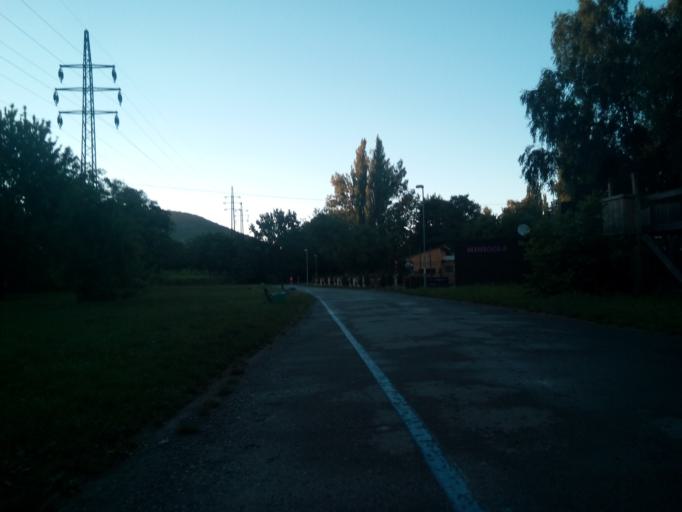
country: SK
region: Kosicky
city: Kosice
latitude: 48.7463
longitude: 21.2536
